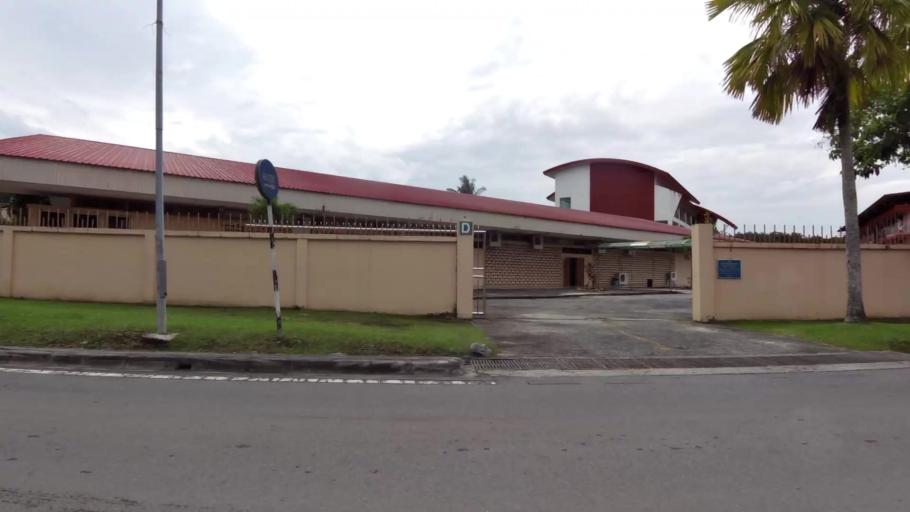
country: BN
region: Brunei and Muara
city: Bandar Seri Begawan
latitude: 4.9026
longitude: 114.9359
